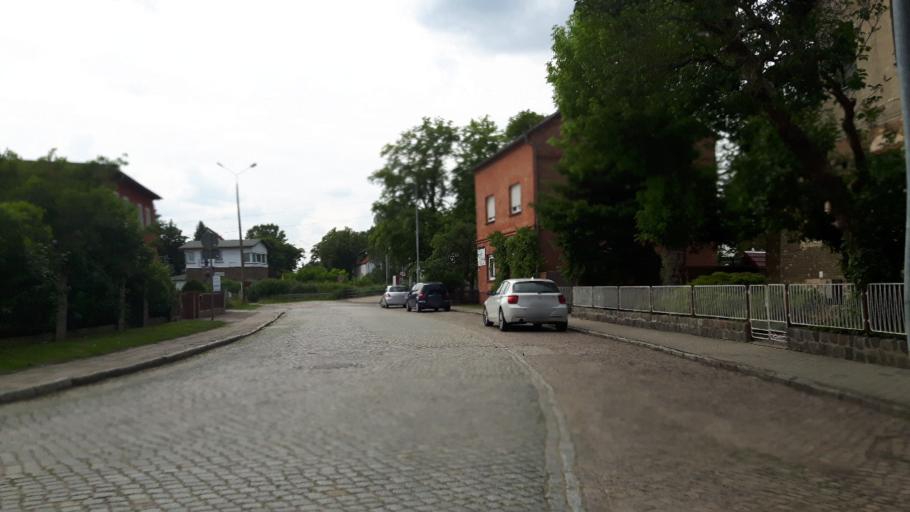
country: DE
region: Saxony-Anhalt
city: Bergwitz
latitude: 51.8026
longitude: 12.5765
